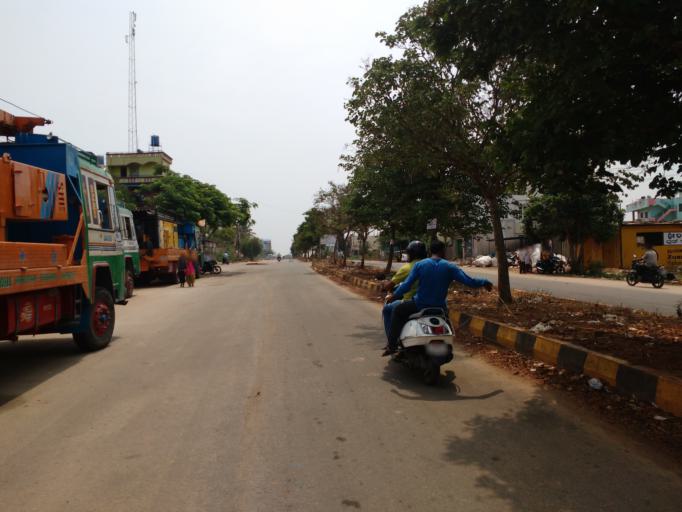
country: IN
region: Karnataka
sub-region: Hassan
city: Hassan
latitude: 13.0269
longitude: 76.1035
